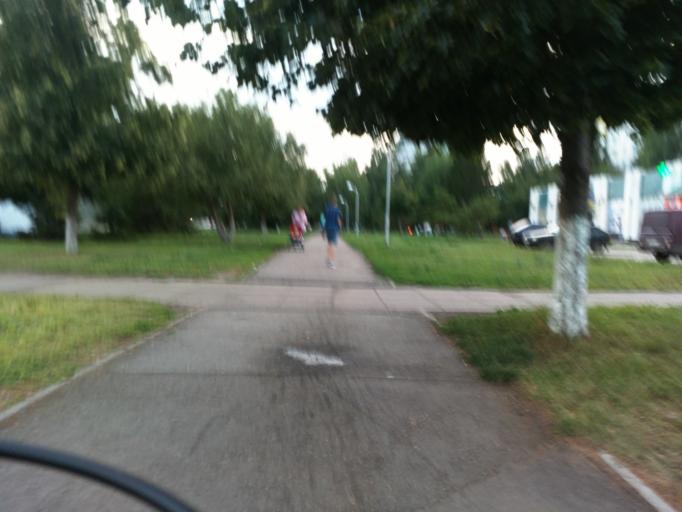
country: RU
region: Tatarstan
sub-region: Tukayevskiy Rayon
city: Naberezhnyye Chelny
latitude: 55.7488
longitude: 52.4168
